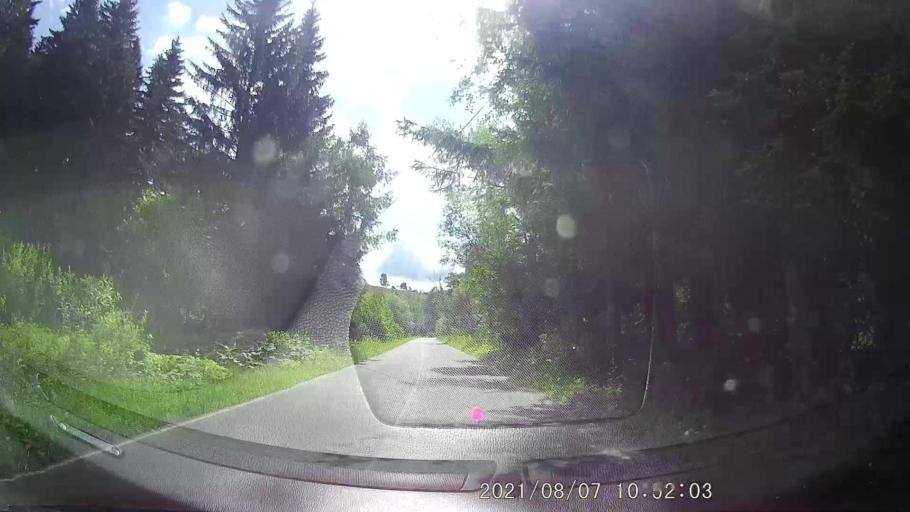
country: CZ
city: Rokytnice v Orlickych Horach
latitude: 50.2845
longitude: 16.4709
